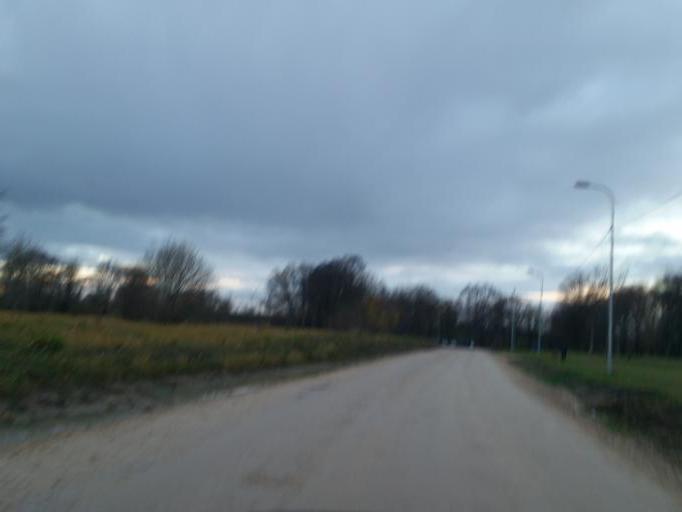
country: LV
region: Riga
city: Riga
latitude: 56.9269
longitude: 24.1165
